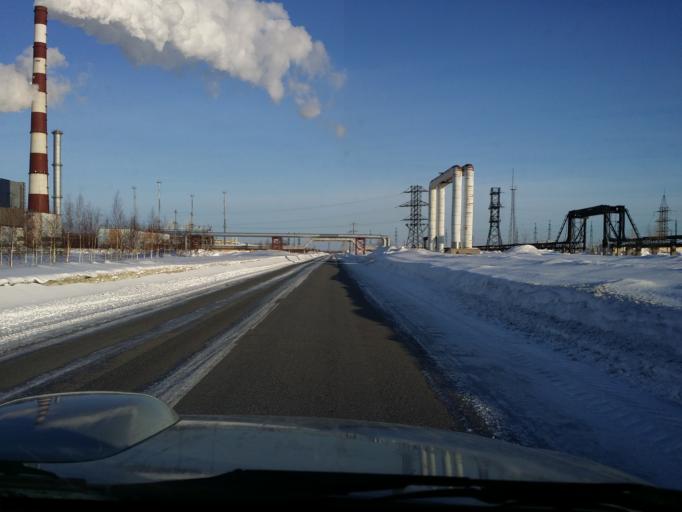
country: RU
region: Khanty-Mansiyskiy Avtonomnyy Okrug
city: Izluchinsk
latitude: 60.9766
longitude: 76.9289
